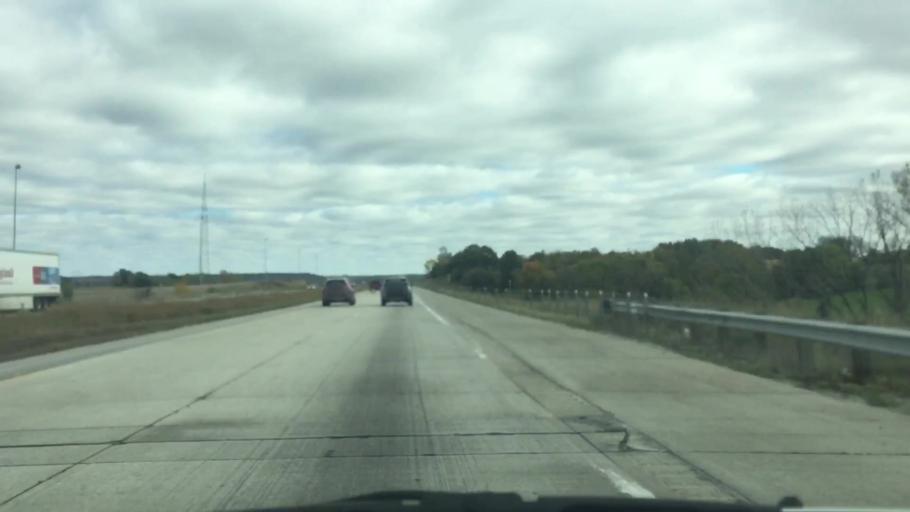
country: US
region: Iowa
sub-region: Polk County
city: Mitchellville
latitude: 41.6807
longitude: -93.3479
